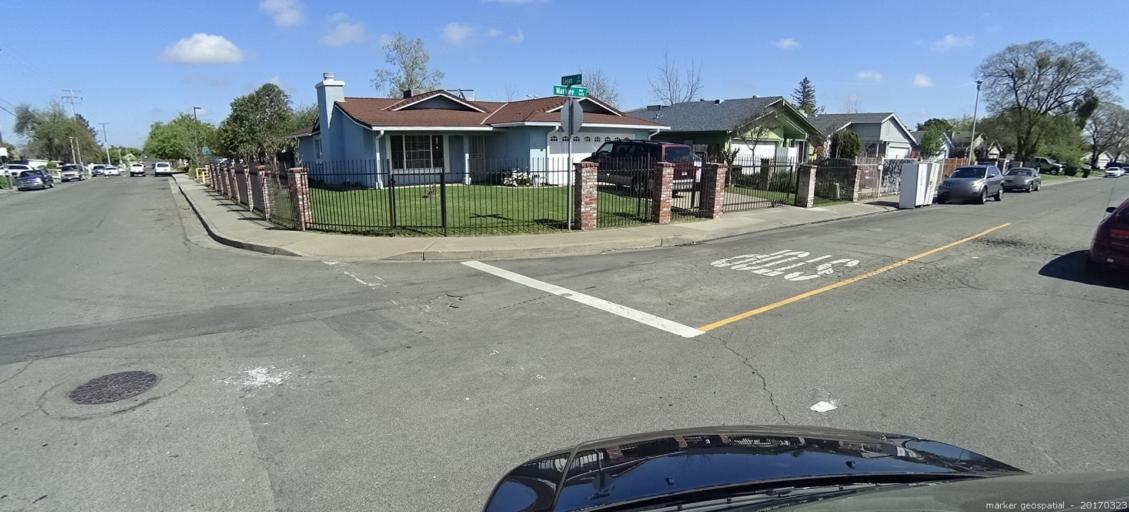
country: US
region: California
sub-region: Sacramento County
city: Florin
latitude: 38.5123
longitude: -121.4152
